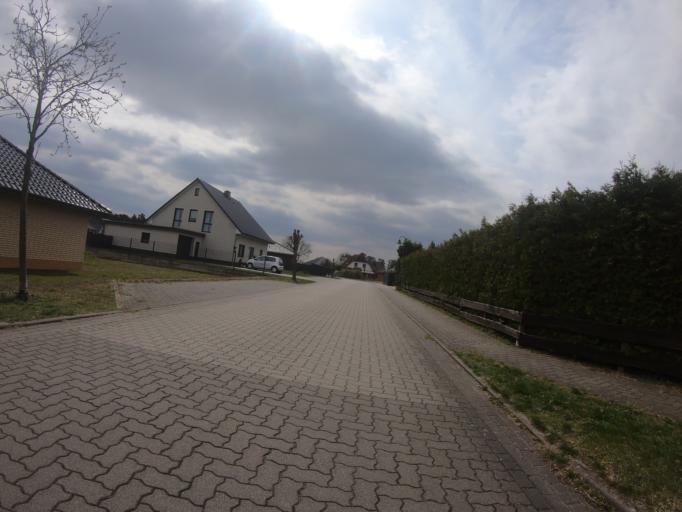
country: DE
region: Lower Saxony
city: Hankensbuttel
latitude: 52.7202
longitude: 10.5995
